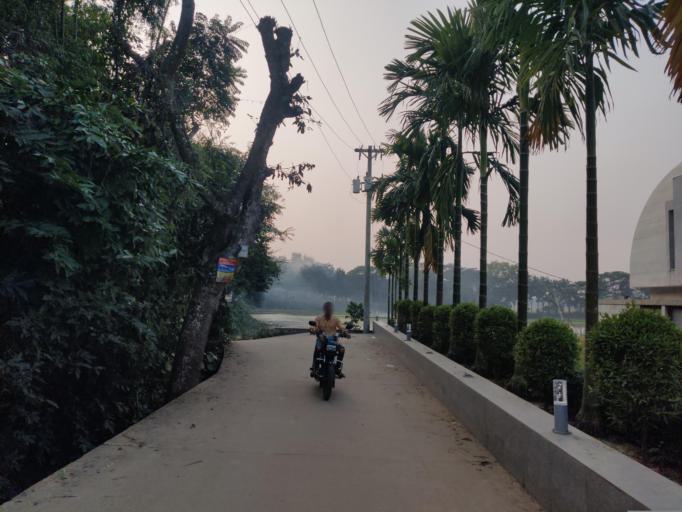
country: BD
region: Dhaka
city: Bajitpur
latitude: 24.1551
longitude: 90.7633
